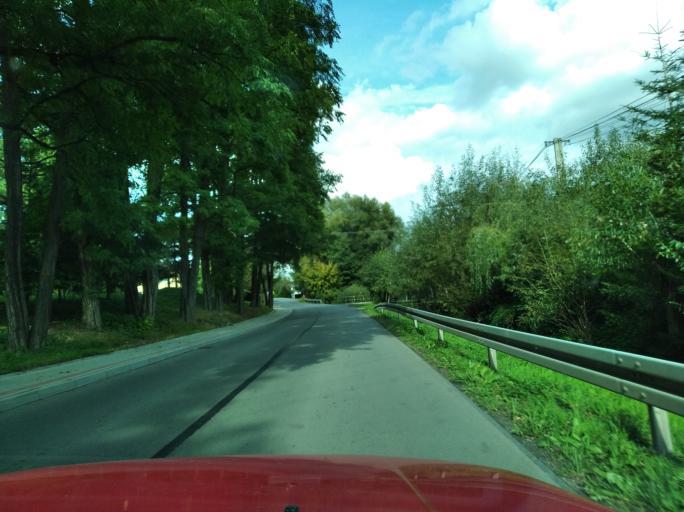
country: PL
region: Subcarpathian Voivodeship
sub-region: Powiat rzeszowski
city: Tyczyn
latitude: 49.9555
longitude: 22.0309
